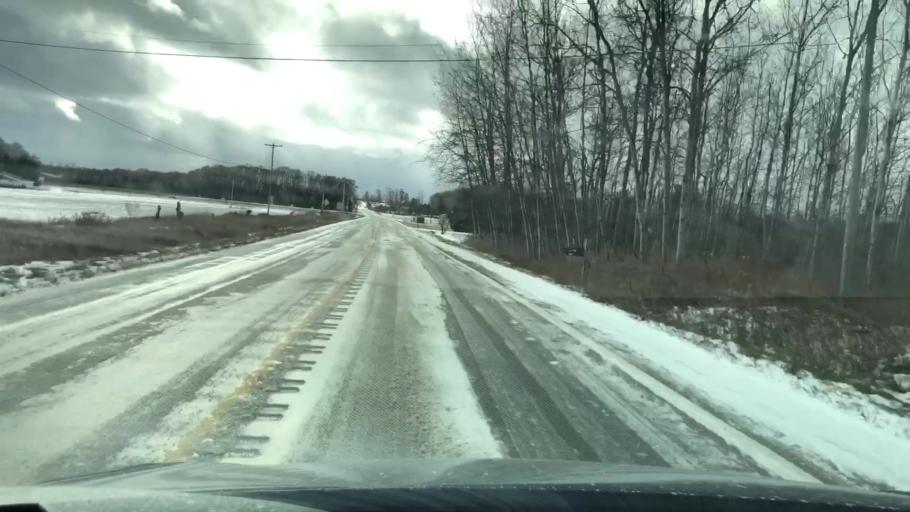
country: US
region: Michigan
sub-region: Antrim County
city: Elk Rapids
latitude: 44.9755
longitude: -85.5047
